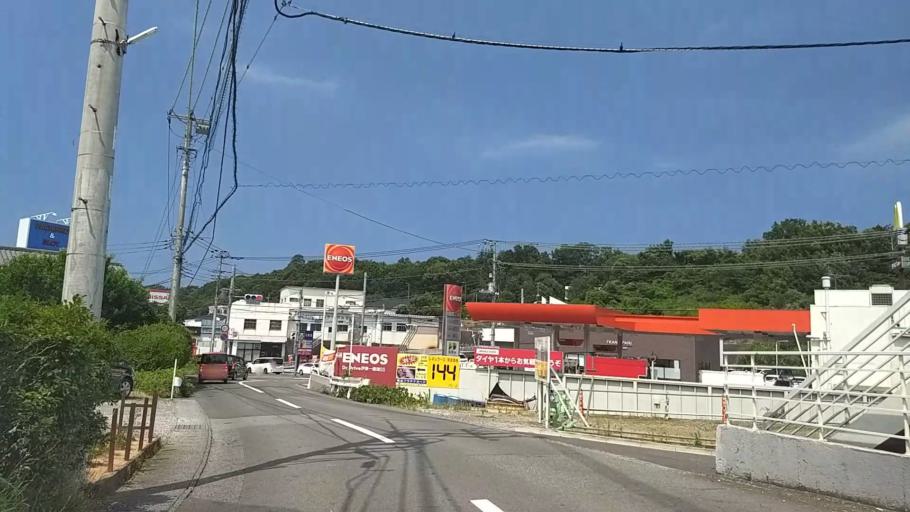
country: JP
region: Shizuoka
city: Ito
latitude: 34.9398
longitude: 139.1166
